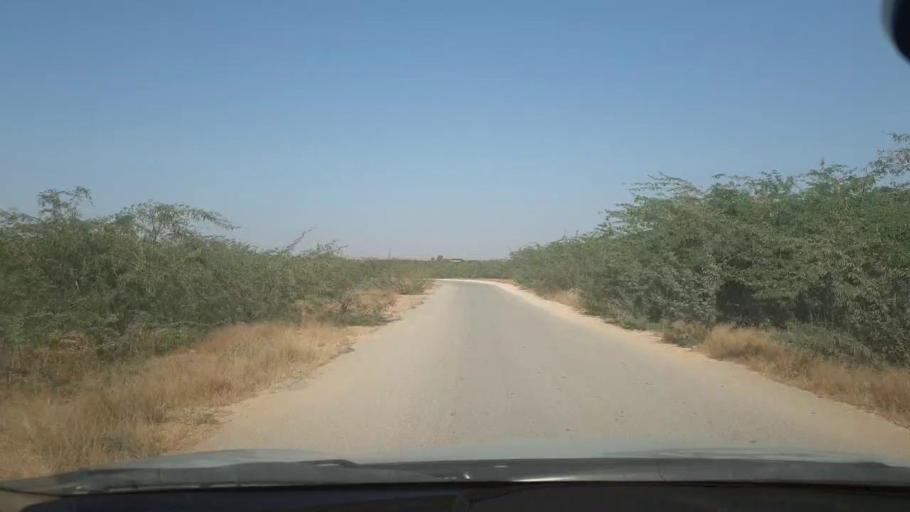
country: PK
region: Sindh
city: Malir Cantonment
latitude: 25.1456
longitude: 67.1662
